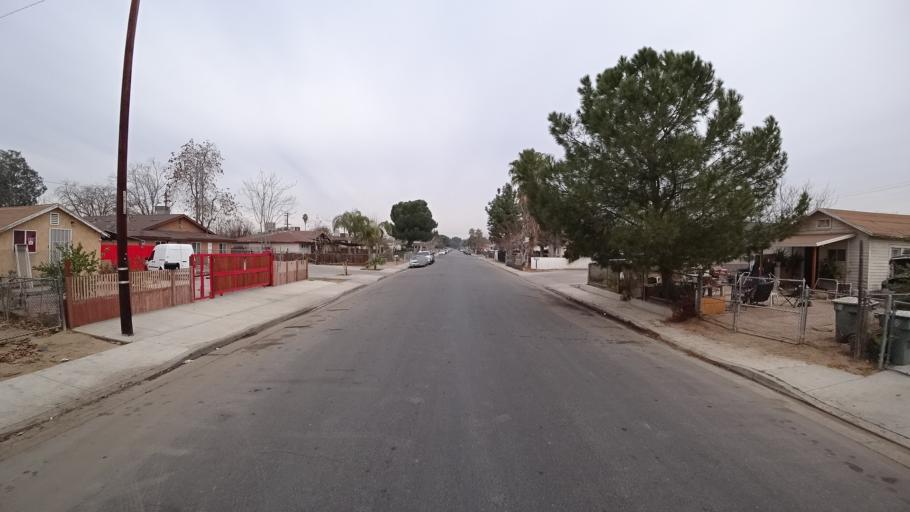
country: US
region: California
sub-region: Kern County
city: Bakersfield
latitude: 35.3566
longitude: -118.9930
